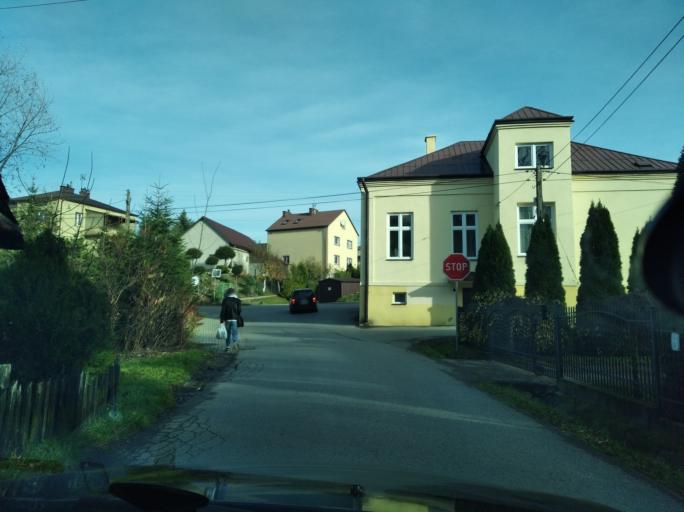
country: PL
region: Subcarpathian Voivodeship
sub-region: Powiat rzeszowski
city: Krasne
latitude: 50.0287
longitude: 22.1065
